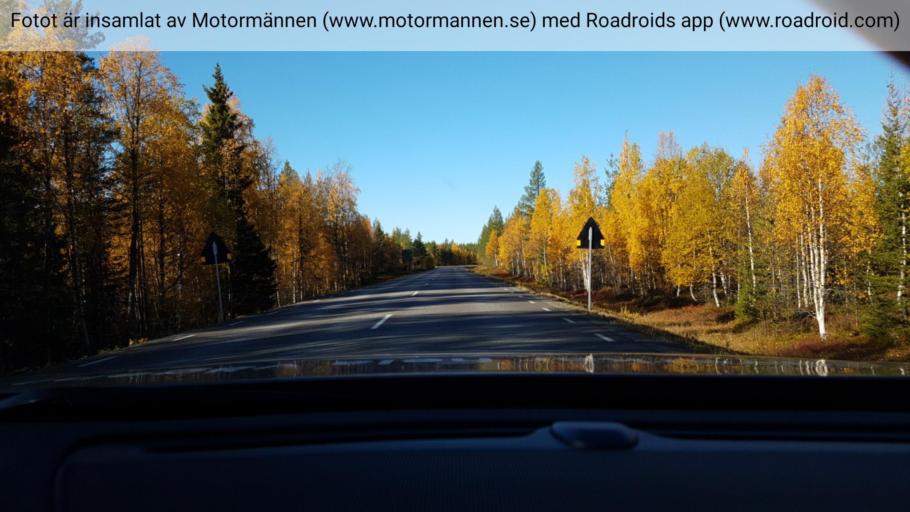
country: SE
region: Vaesterbotten
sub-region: Norsjo Kommun
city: Norsjoe
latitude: 65.4099
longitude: 19.7547
